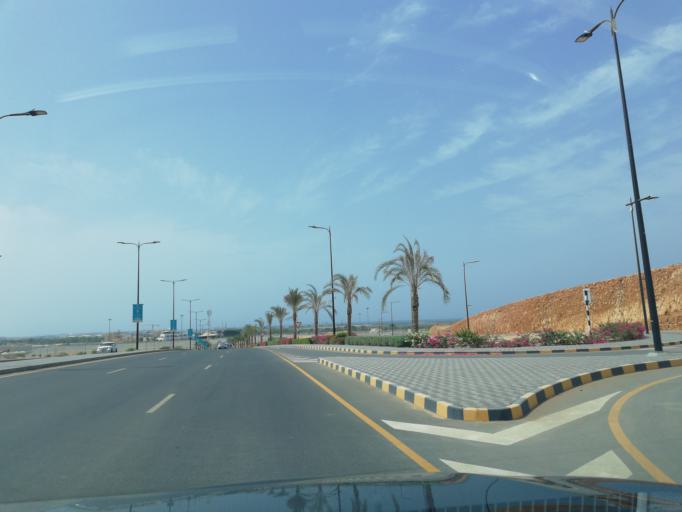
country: OM
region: Muhafazat Masqat
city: Bawshar
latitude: 23.5783
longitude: 58.3231
